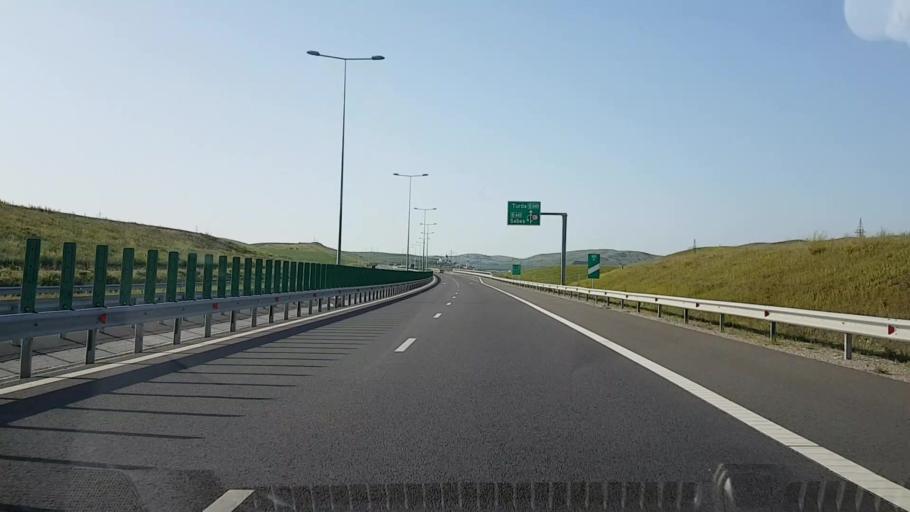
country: RO
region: Alba
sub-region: Comuna Unirea
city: Unirea
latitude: 46.4157
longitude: 23.7999
